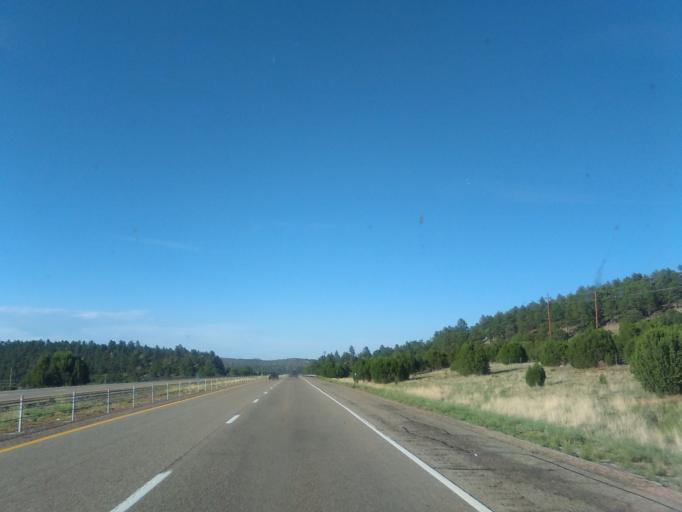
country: US
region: New Mexico
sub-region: San Miguel County
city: Las Vegas
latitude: 35.5043
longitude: -105.2610
